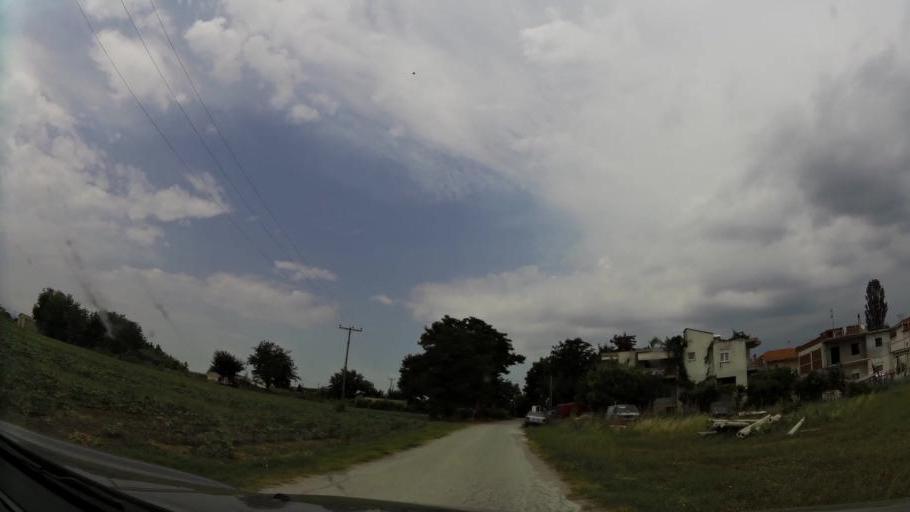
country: GR
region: Central Macedonia
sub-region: Nomos Pierias
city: Kallithea
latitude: 40.2746
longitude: 22.5702
